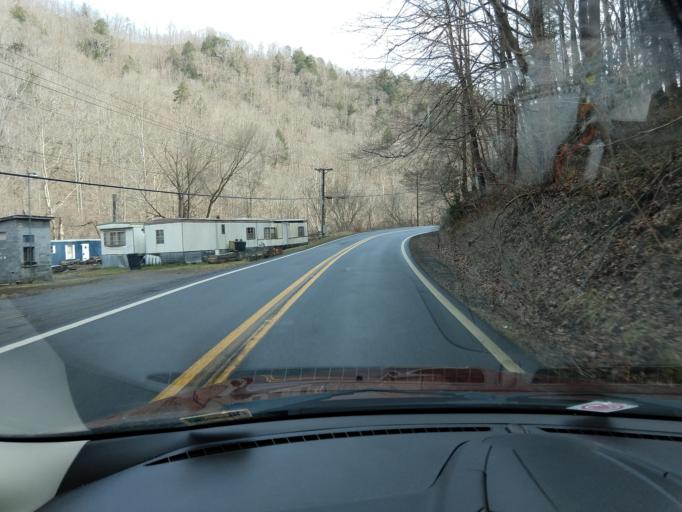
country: US
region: West Virginia
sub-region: McDowell County
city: Welch
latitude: 37.3401
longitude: -81.7525
